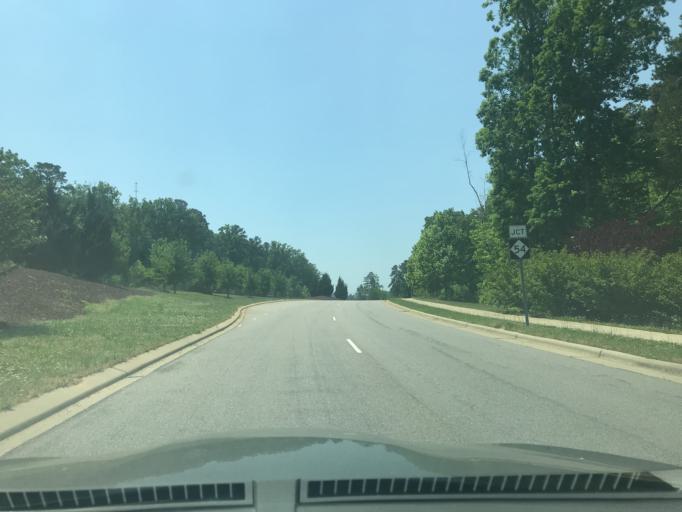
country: US
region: North Carolina
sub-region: Wake County
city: Cary
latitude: 35.7924
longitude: -78.7272
